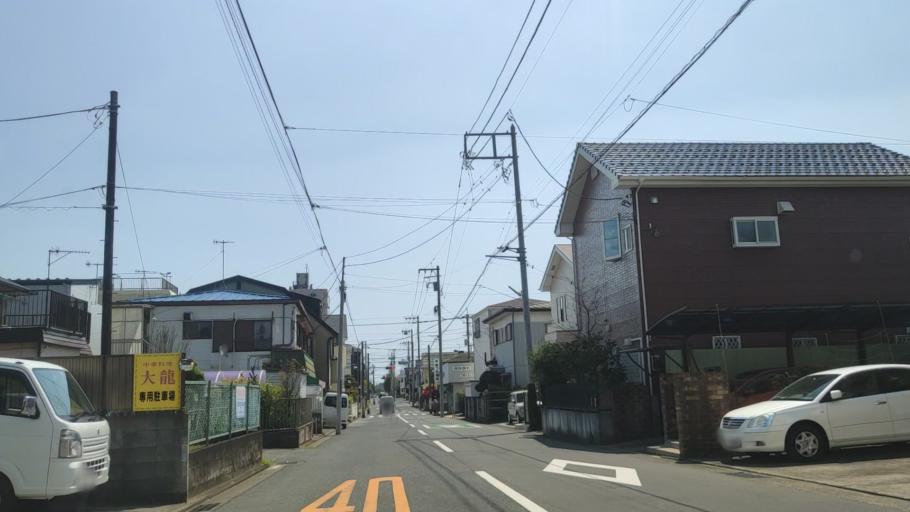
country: JP
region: Kanagawa
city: Hiratsuka
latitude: 35.3329
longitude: 139.3355
